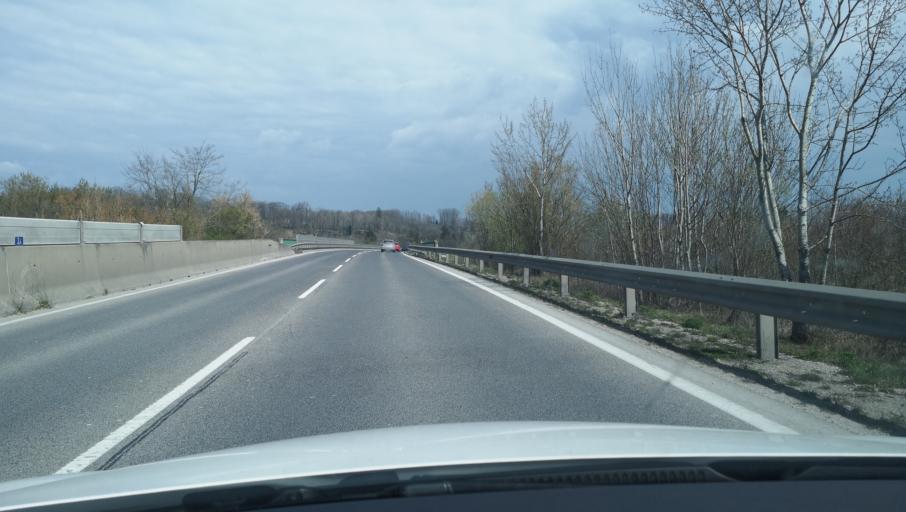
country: AT
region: Lower Austria
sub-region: Politischer Bezirk Amstetten
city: Winklarn
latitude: 48.1101
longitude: 14.8377
